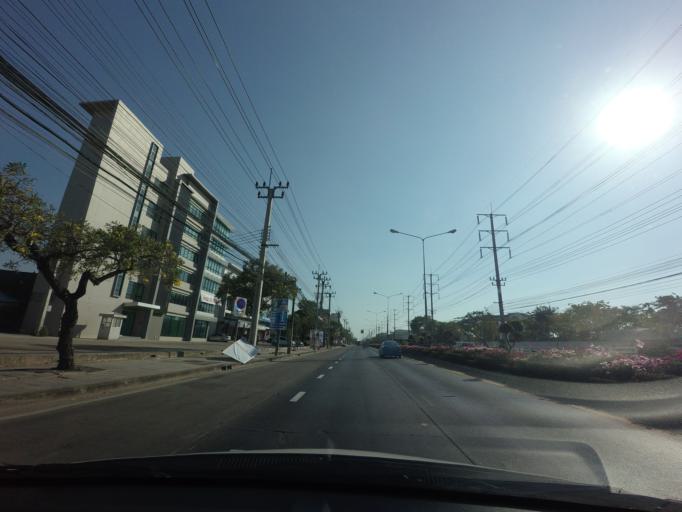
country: TH
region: Bangkok
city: Nong Chok
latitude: 13.8495
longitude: 100.8598
